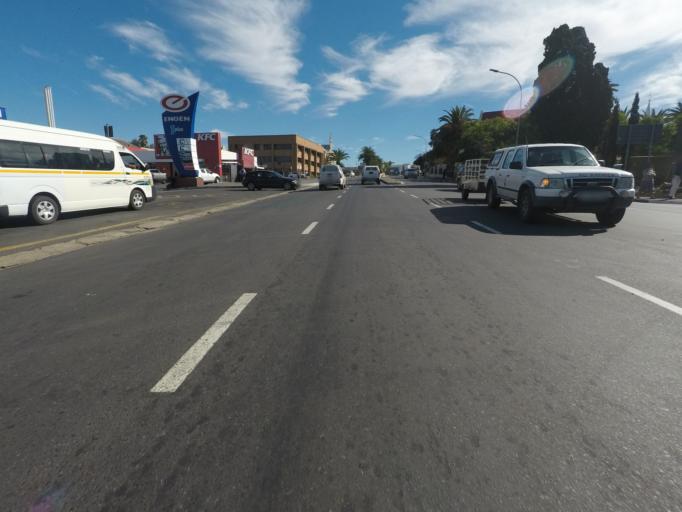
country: ZA
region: Western Cape
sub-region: West Coast District Municipality
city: Malmesbury
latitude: -33.4647
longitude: 18.7290
